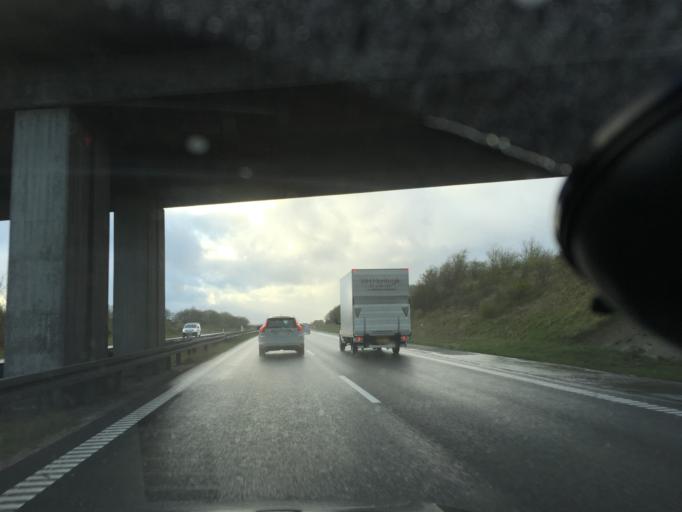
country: DK
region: North Denmark
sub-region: Mariagerfjord Kommune
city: Hobro
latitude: 56.5901
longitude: 9.7721
